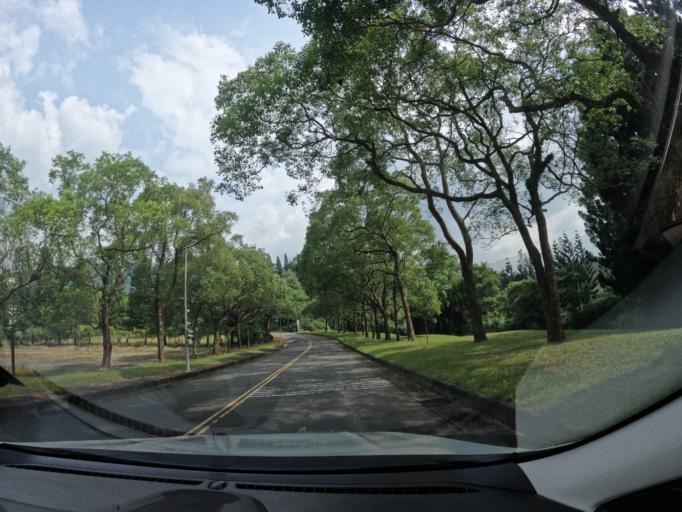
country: TW
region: Taiwan
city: Daxi
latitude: 24.8834
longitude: 121.3236
